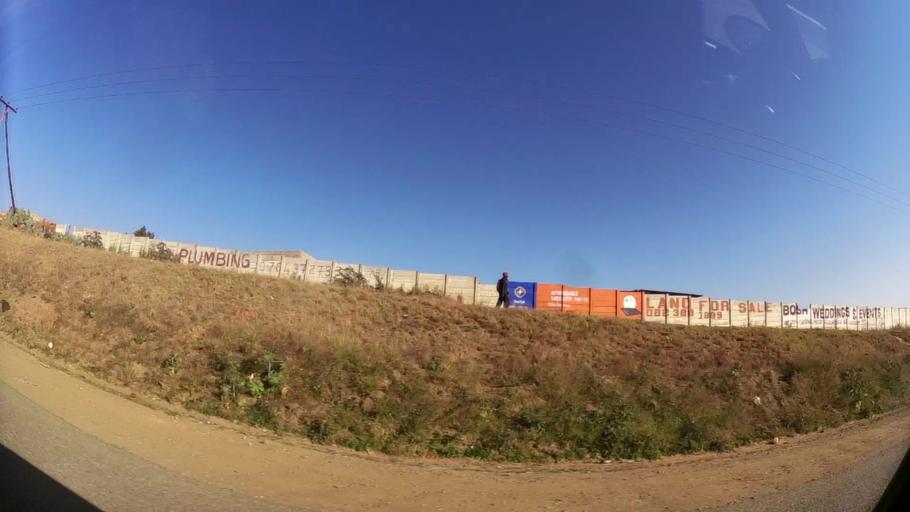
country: ZA
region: Gauteng
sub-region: City of Tshwane Metropolitan Municipality
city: Centurion
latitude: -25.8987
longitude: 28.1030
